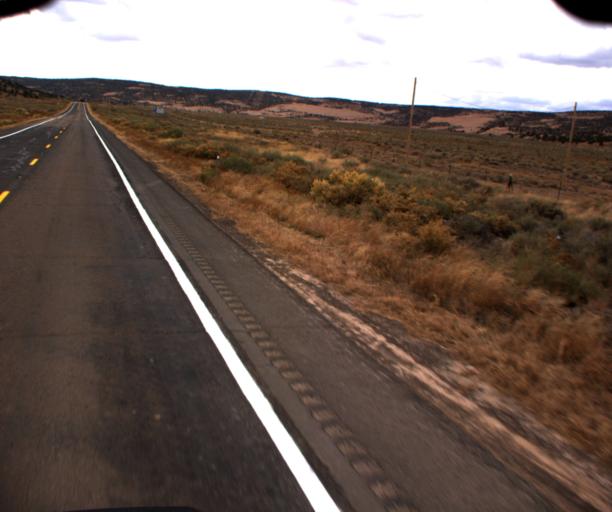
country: US
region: Arizona
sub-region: Navajo County
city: Kayenta
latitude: 36.6272
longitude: -110.4559
